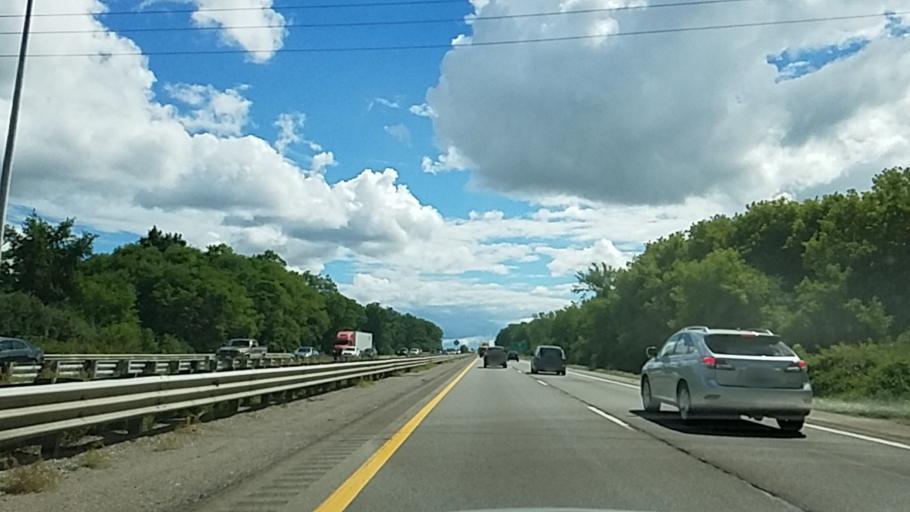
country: US
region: Michigan
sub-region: Washtenaw County
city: Ann Arbor
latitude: 42.3305
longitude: -83.7432
